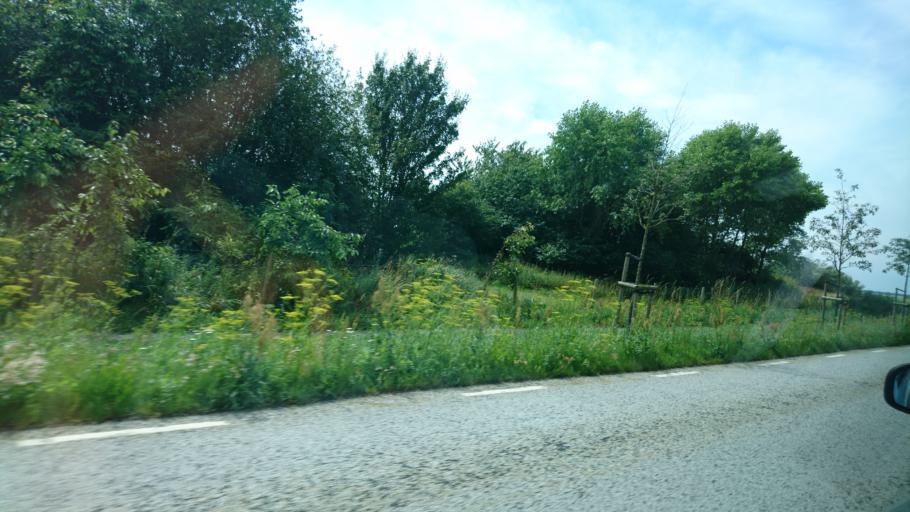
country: SE
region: Skane
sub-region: Skurups Kommun
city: Skivarp
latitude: 55.3880
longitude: 13.5345
